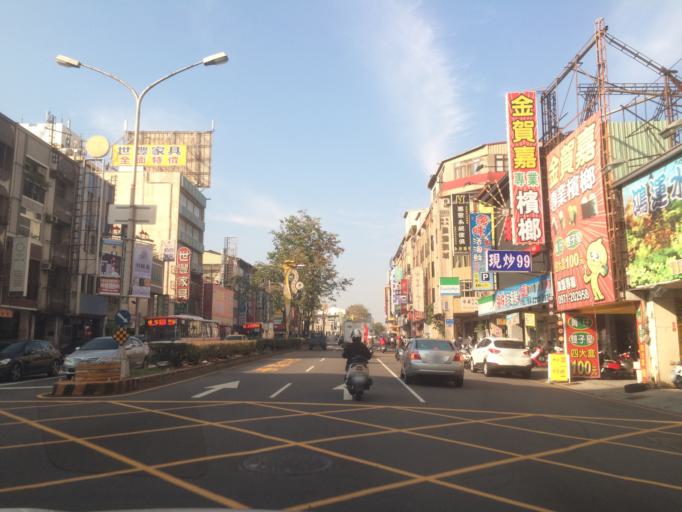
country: TW
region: Taiwan
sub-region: Taichung City
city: Taichung
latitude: 24.1688
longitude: 120.6728
